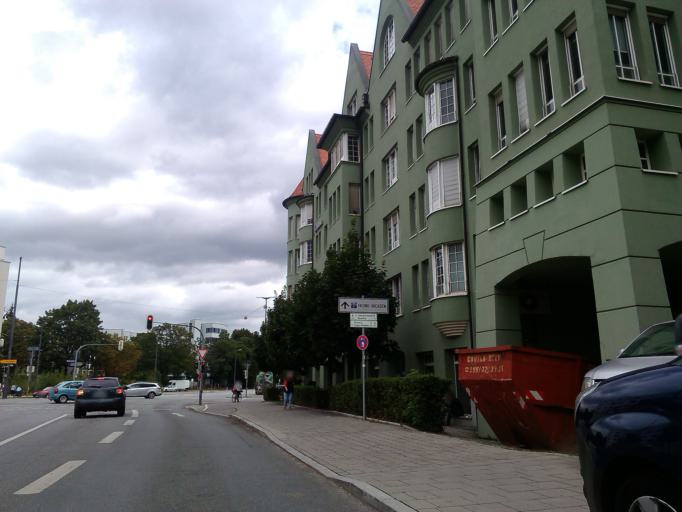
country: DE
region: Bavaria
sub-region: Upper Bavaria
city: Pasing
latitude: 48.1463
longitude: 11.4532
